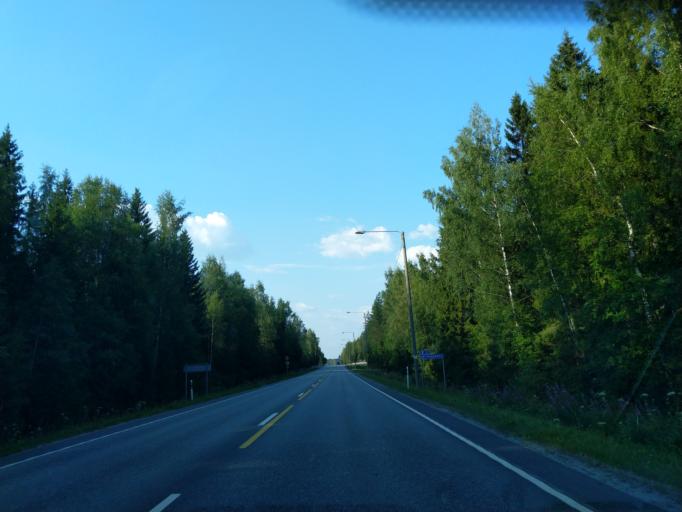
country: FI
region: Satakunta
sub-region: Pori
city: Pomarkku
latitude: 61.6877
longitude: 21.9961
